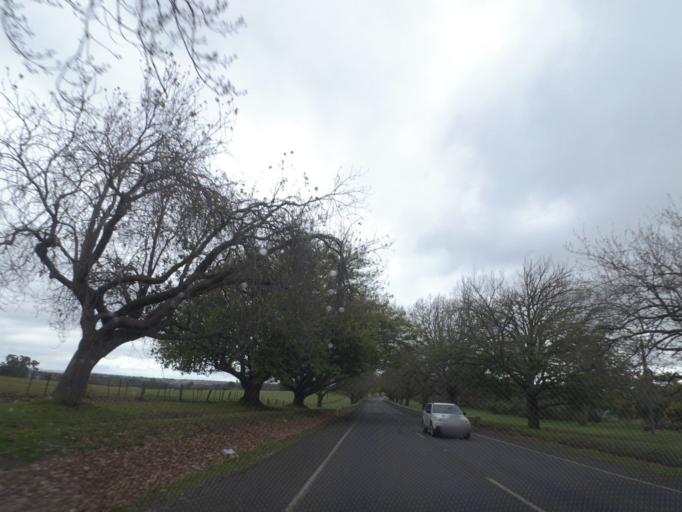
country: AU
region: Victoria
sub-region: Hume
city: Sunbury
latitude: -37.3399
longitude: 144.5274
